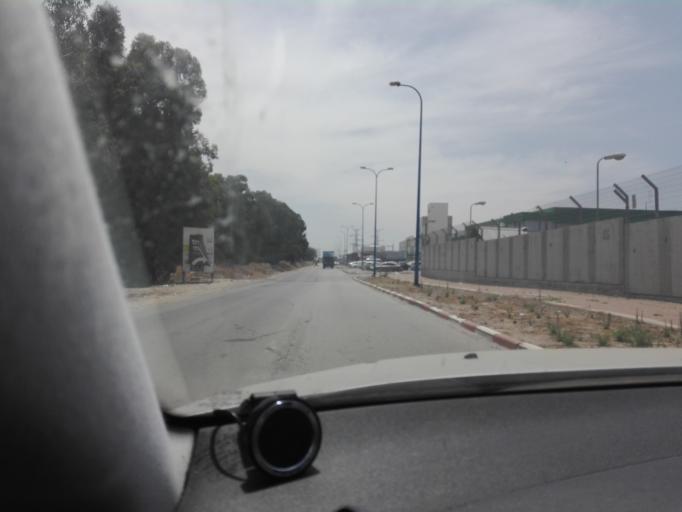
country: IL
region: Central District
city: Bene 'Ayish
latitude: 31.7256
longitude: 34.7551
